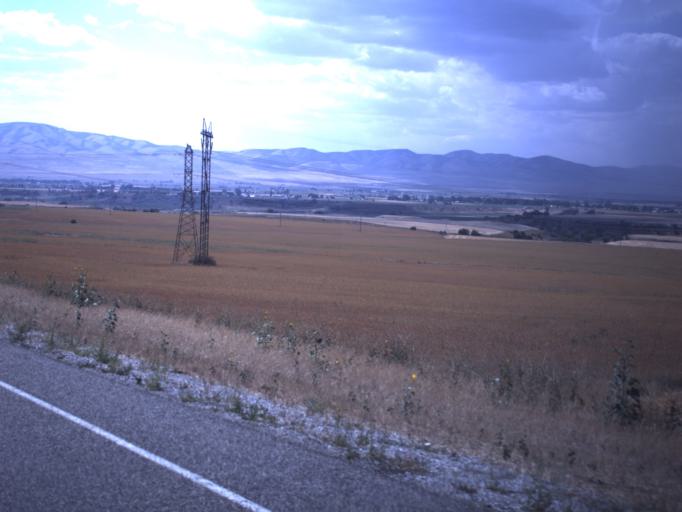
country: US
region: Utah
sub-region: Box Elder County
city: Garland
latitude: 41.7920
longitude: -112.0667
